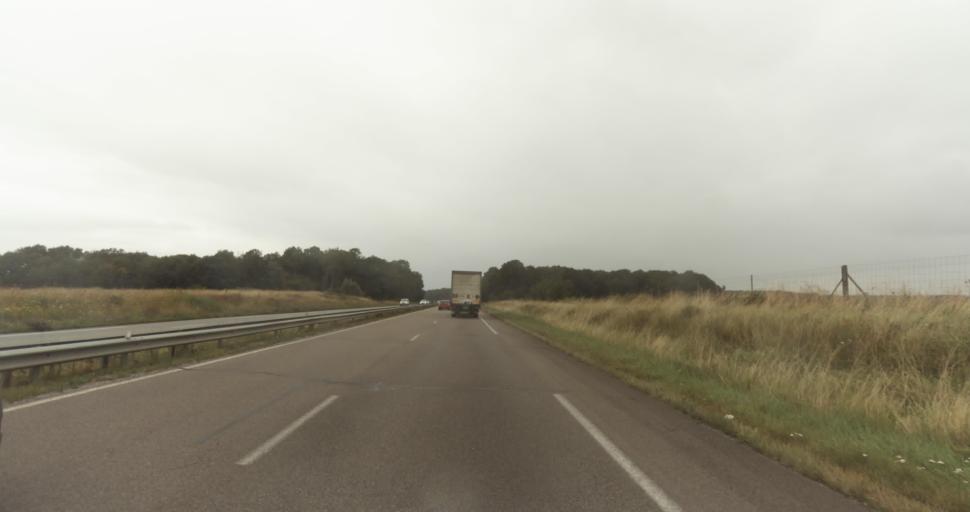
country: FR
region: Haute-Normandie
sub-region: Departement de l'Eure
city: Normanville
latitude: 49.0986
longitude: 1.1889
